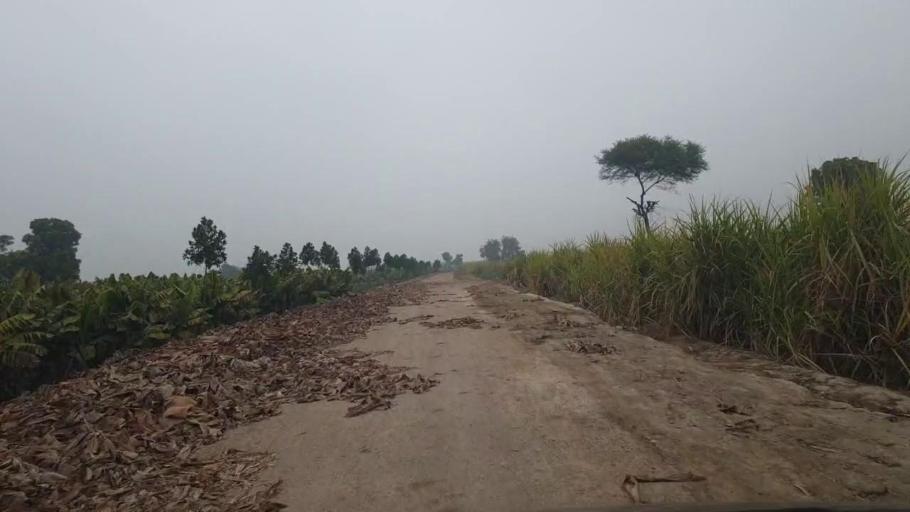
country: PK
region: Sindh
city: Tando Adam
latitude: 25.8066
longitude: 68.6655
